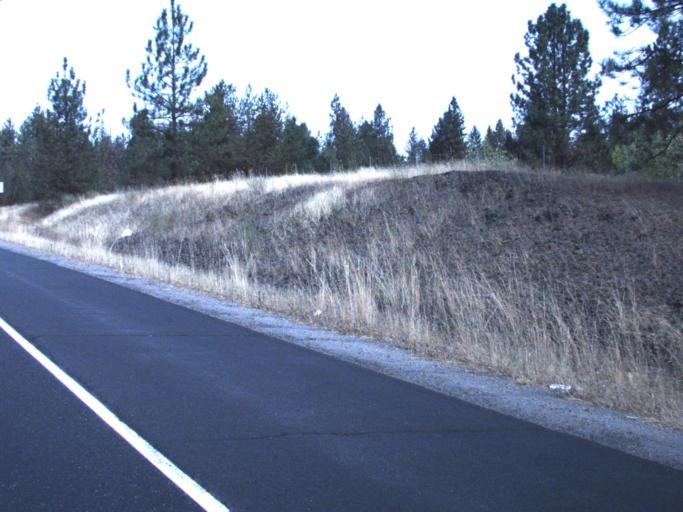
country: US
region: Washington
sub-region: Spokane County
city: Deer Park
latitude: 47.9294
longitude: -117.4646
